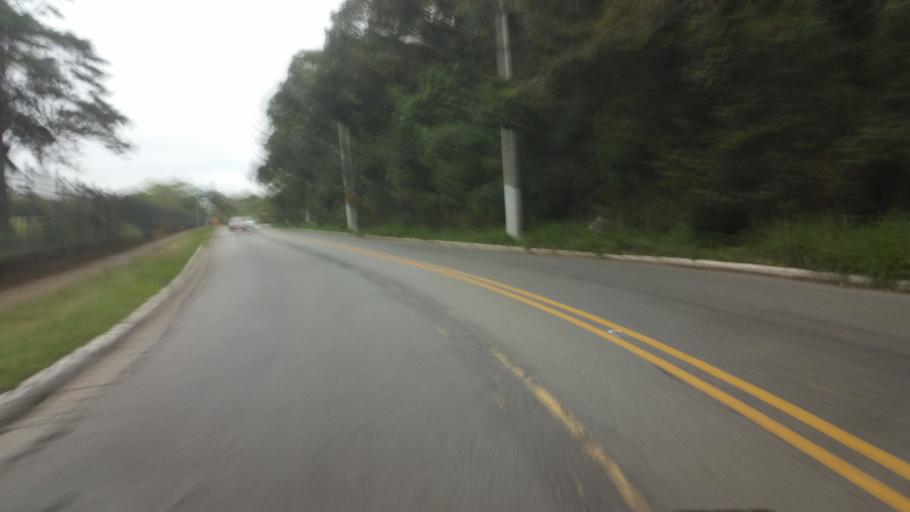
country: BR
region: Sao Paulo
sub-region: Diadema
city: Diadema
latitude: -23.6410
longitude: -46.6274
